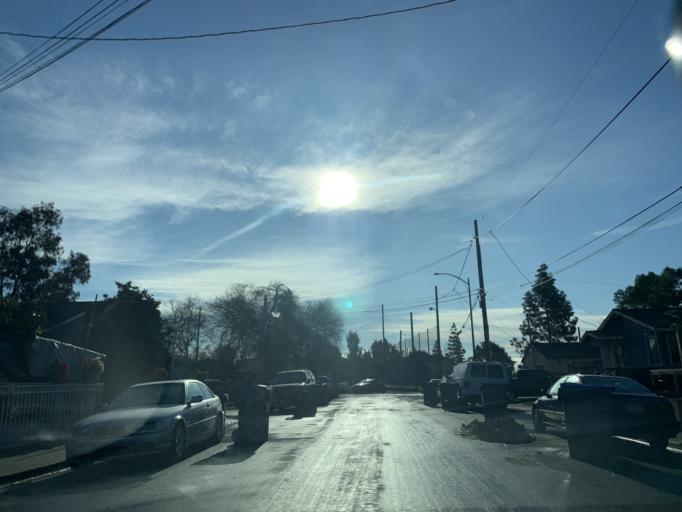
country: US
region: California
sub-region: Santa Clara County
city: Alum Rock
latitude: 37.3472
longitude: -121.8558
